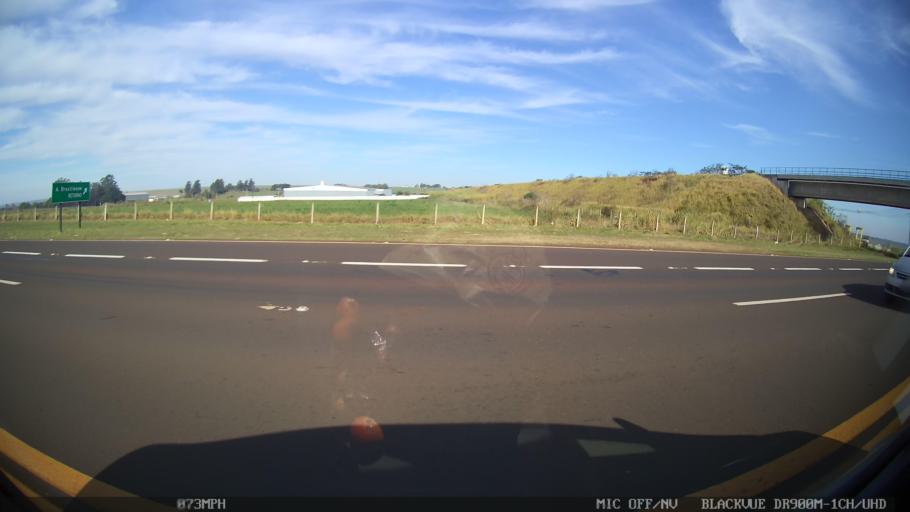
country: BR
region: Sao Paulo
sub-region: Americo Brasiliense
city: Americo Brasiliense
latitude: -21.7770
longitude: -48.1042
